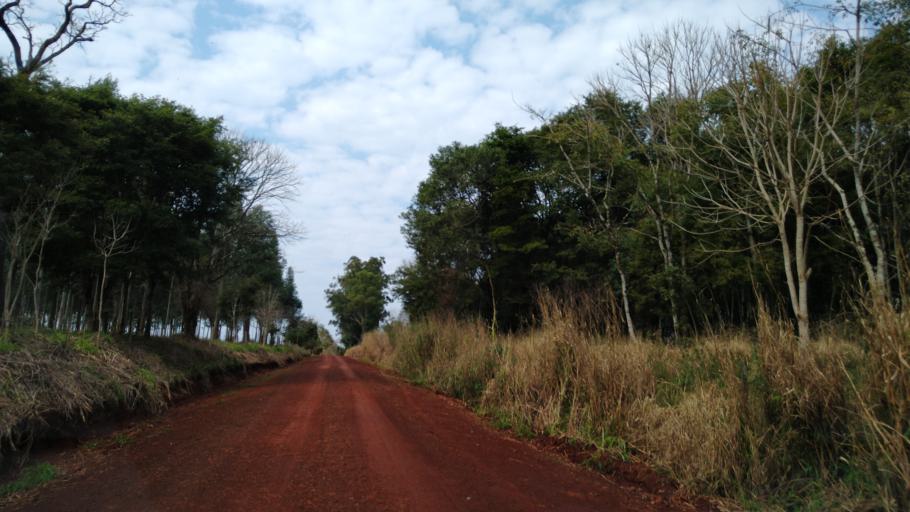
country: AR
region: Misiones
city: Capiovi
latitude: -26.9517
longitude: -55.0663
